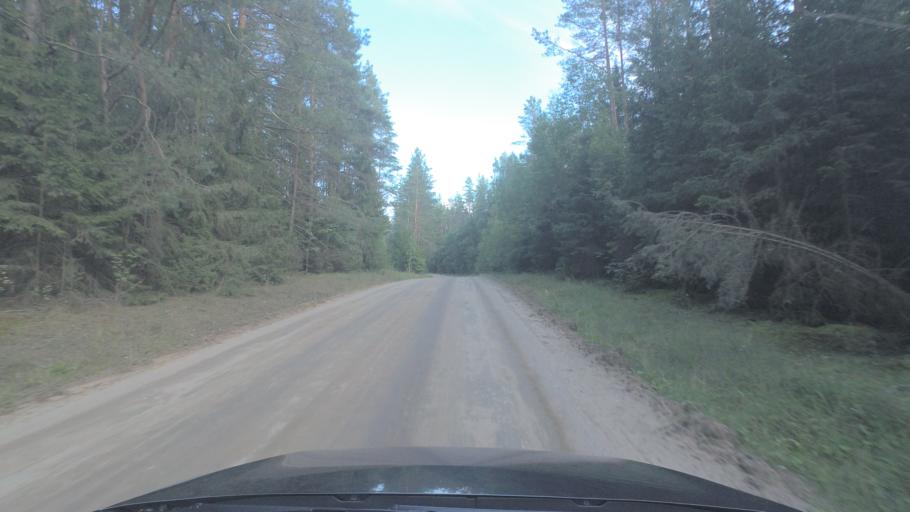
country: LT
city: Svencioneliai
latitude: 55.1621
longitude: 25.8484
